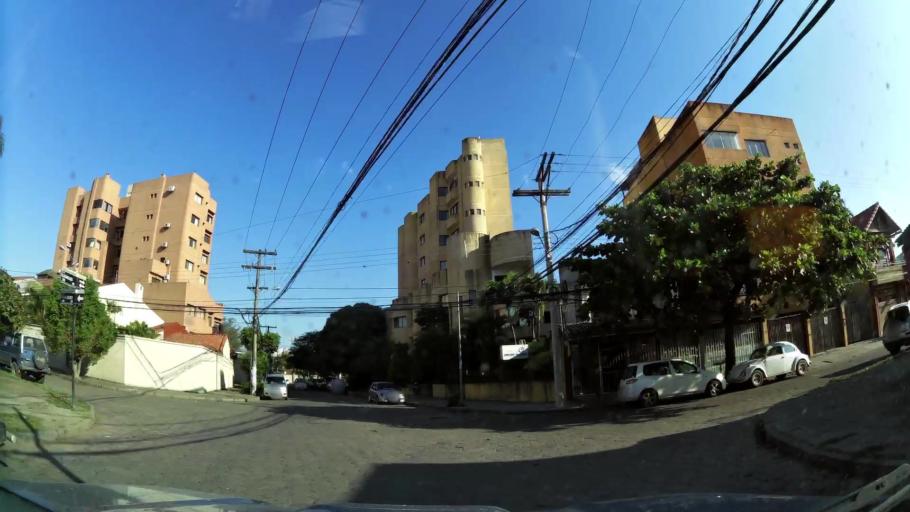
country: BO
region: Santa Cruz
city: Santa Cruz de la Sierra
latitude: -17.7732
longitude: -63.1867
